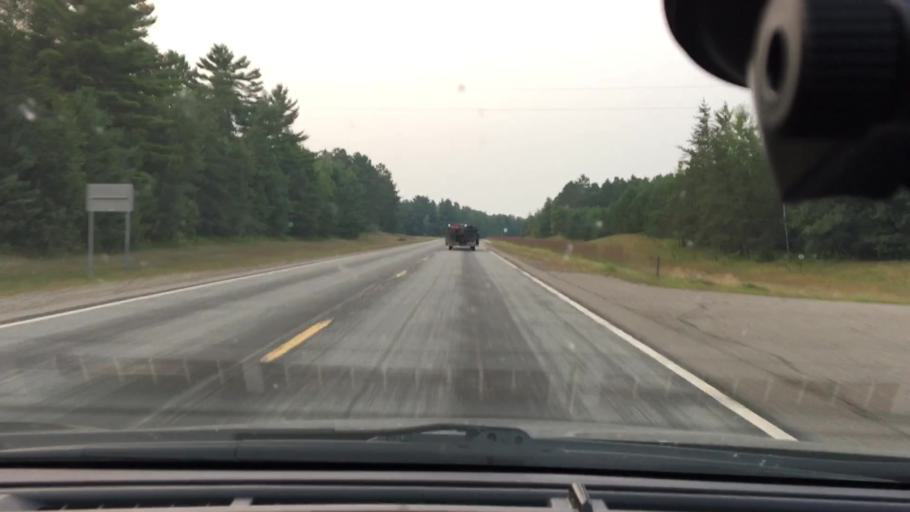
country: US
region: Minnesota
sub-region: Crow Wing County
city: Cross Lake
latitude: 46.7070
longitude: -93.9559
